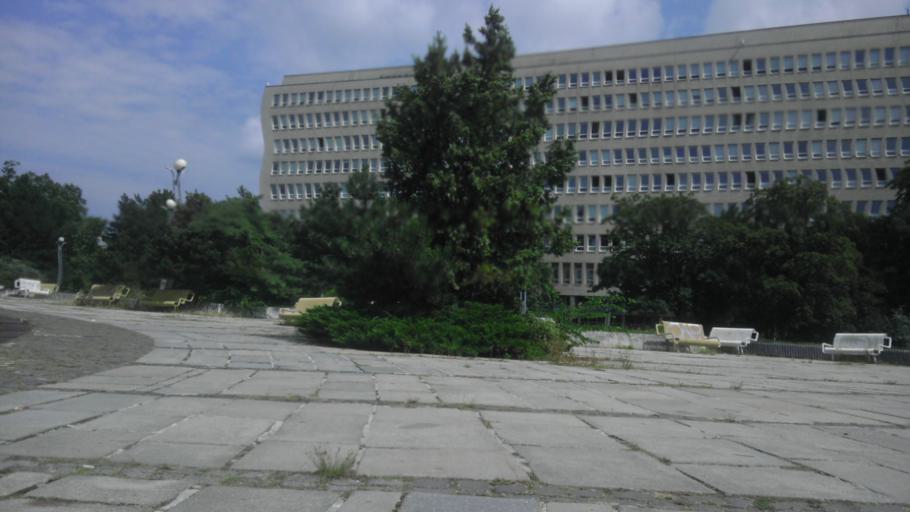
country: SK
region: Bratislavsky
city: Bratislava
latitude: 48.1520
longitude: 17.1120
